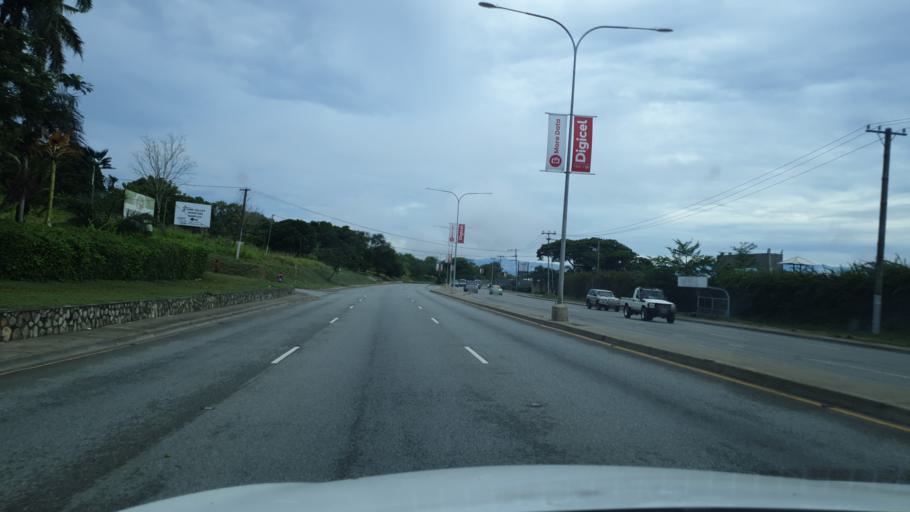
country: PG
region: National Capital
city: Port Moresby
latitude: -9.4336
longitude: 147.1794
